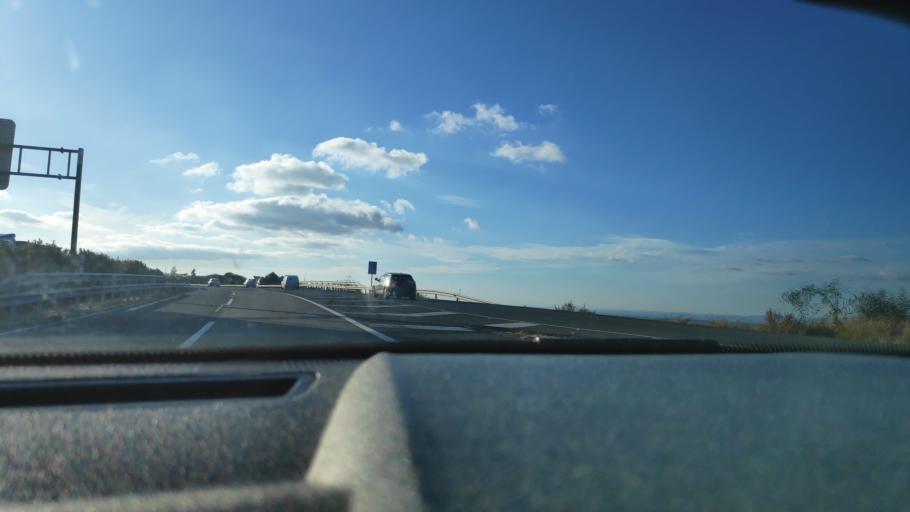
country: ES
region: Andalusia
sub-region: Provincia de Sevilla
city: Carmona
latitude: 37.4886
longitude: -5.6422
